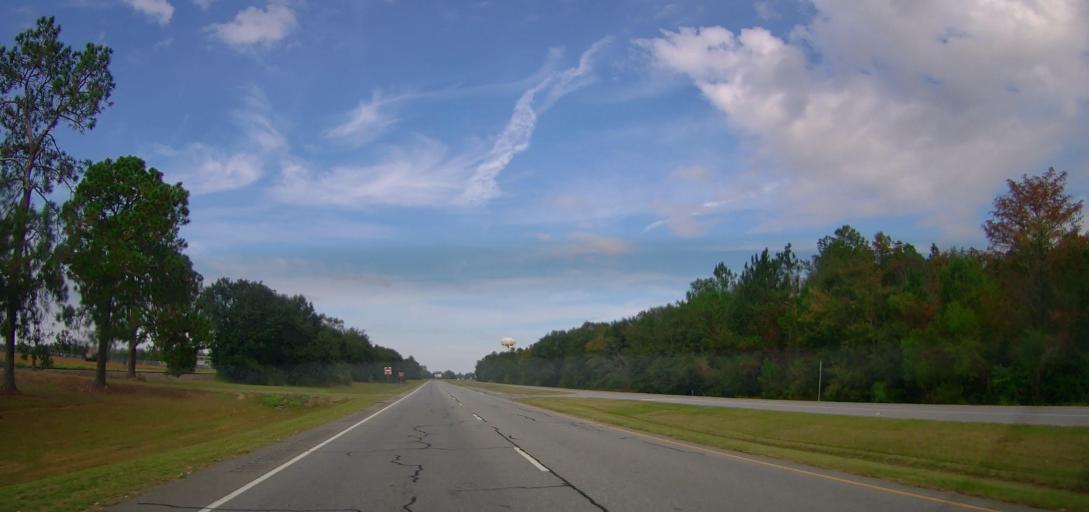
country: US
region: Georgia
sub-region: Mitchell County
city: Camilla
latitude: 31.2658
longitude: -84.1940
